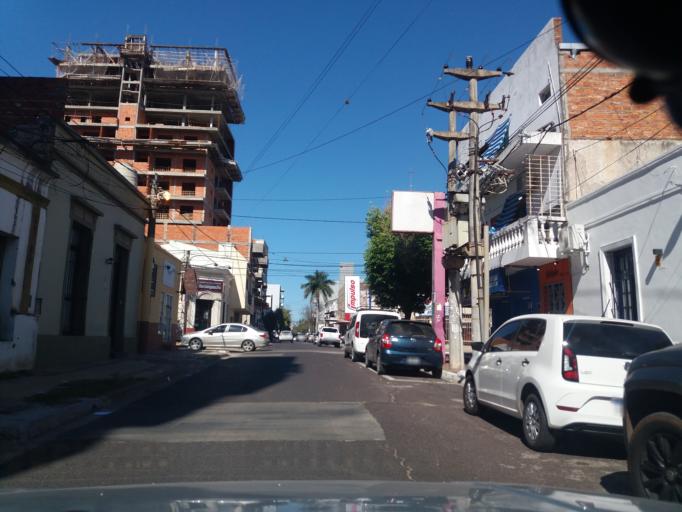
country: AR
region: Corrientes
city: Corrientes
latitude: -27.4702
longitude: -58.8419
